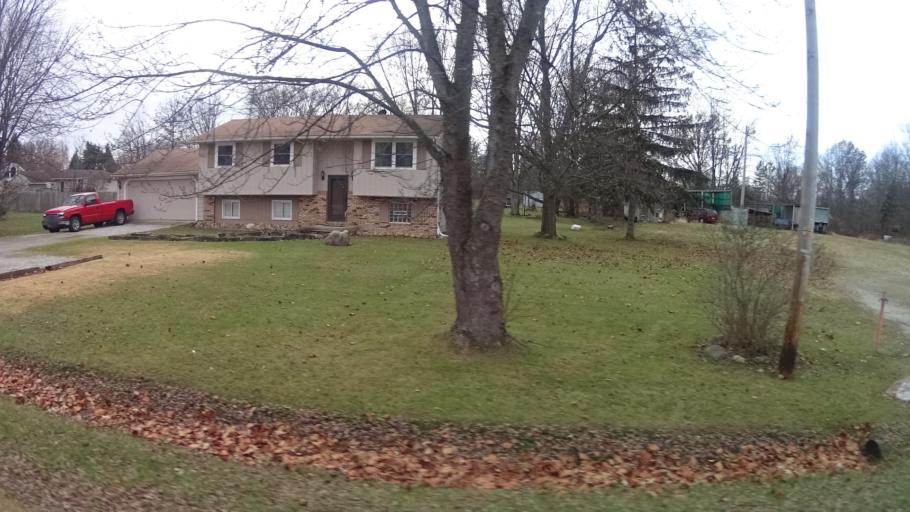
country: US
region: Ohio
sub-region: Lorain County
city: North Ridgeville
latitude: 41.3748
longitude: -82.0030
